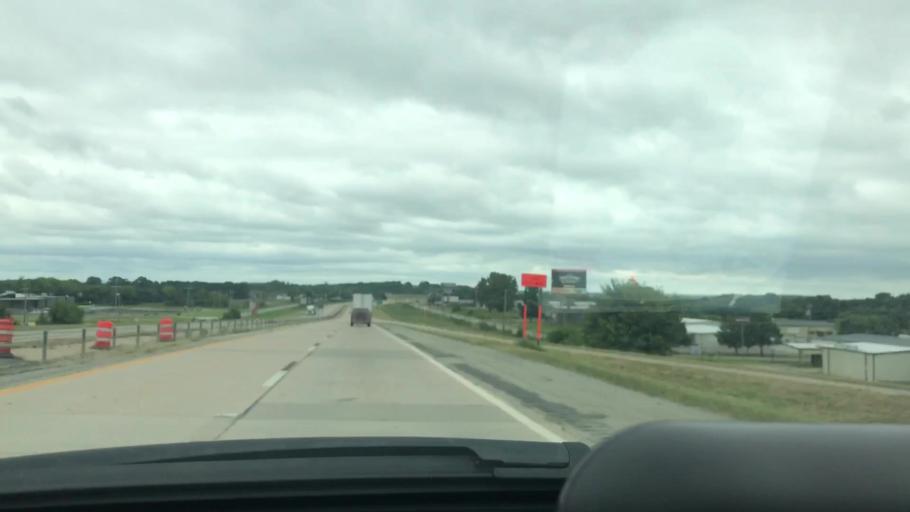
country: US
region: Oklahoma
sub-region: McIntosh County
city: Eufaula
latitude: 35.2963
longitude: -95.5931
